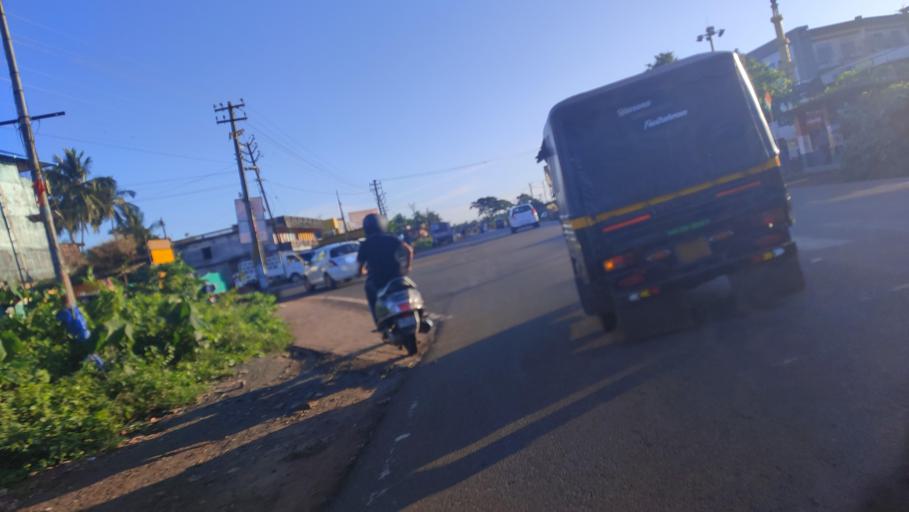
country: IN
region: Kerala
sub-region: Kasaragod District
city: Kasaragod
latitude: 12.4649
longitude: 75.0582
